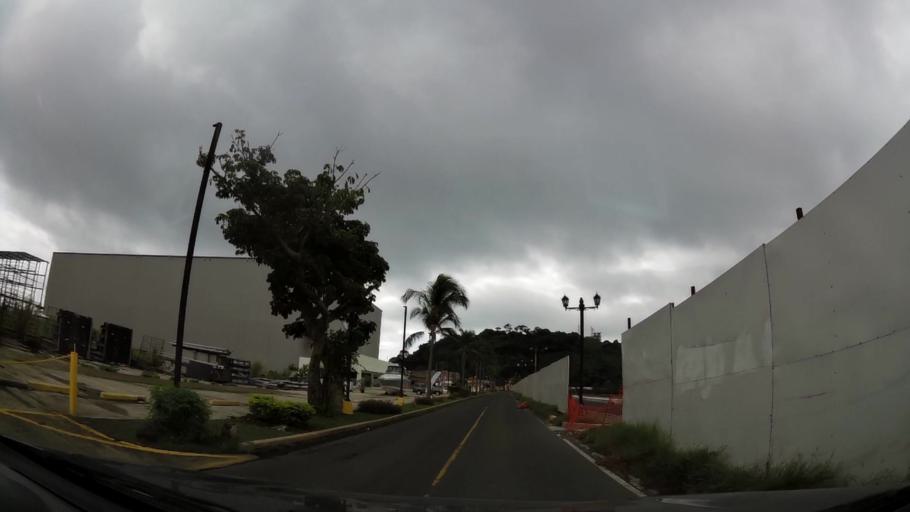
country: PA
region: Panama
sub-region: Distrito de Panama
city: Ancon
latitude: 8.9123
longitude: -79.5243
